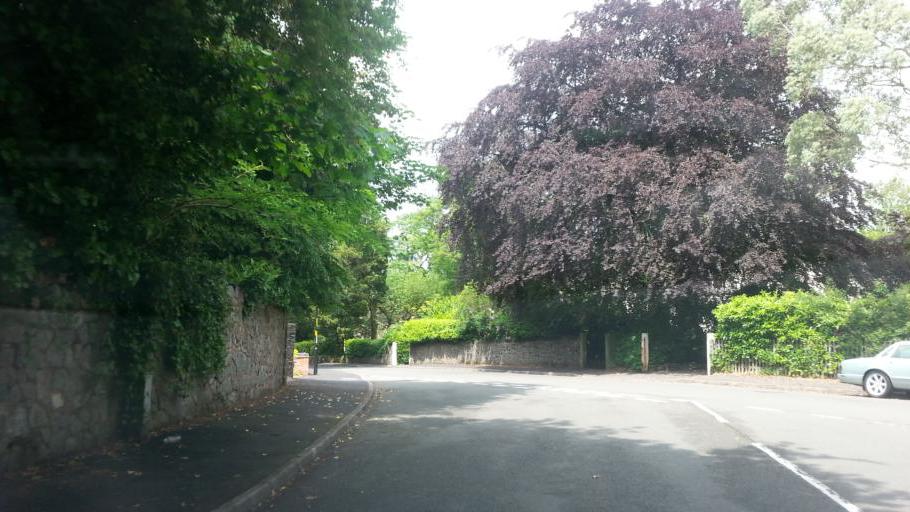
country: GB
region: England
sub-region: City and Borough of Birmingham
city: Birmingham
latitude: 52.4618
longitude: -1.9157
